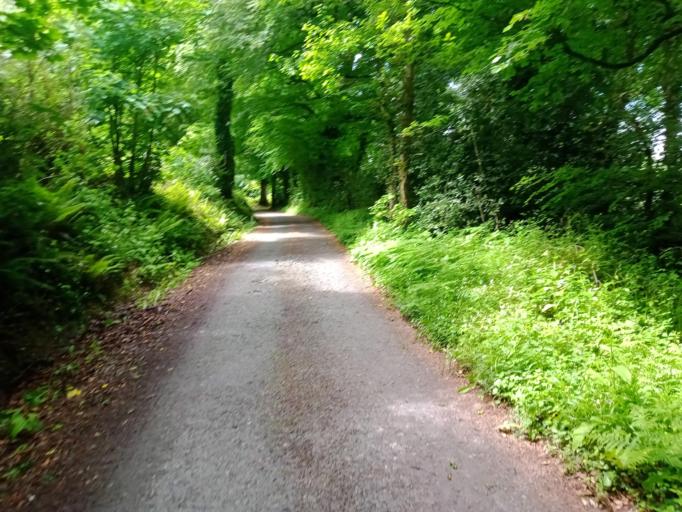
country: IE
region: Leinster
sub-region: Kilkenny
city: Thomastown
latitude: 52.4766
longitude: -7.0531
